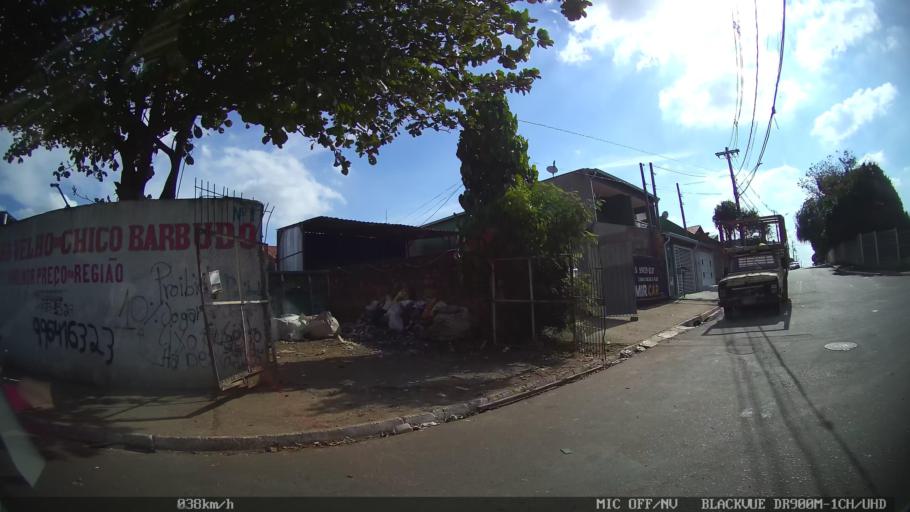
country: BR
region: Sao Paulo
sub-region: Hortolandia
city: Hortolandia
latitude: -22.8925
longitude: -47.2392
